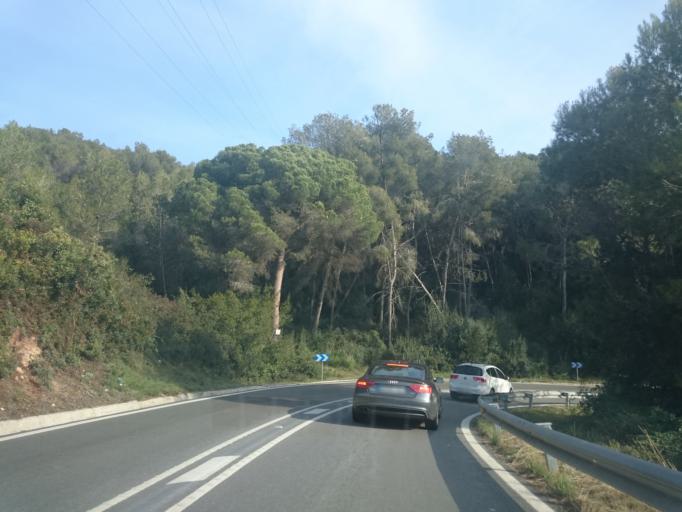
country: ES
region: Catalonia
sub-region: Provincia de Barcelona
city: Gava
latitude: 41.3086
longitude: 1.9828
